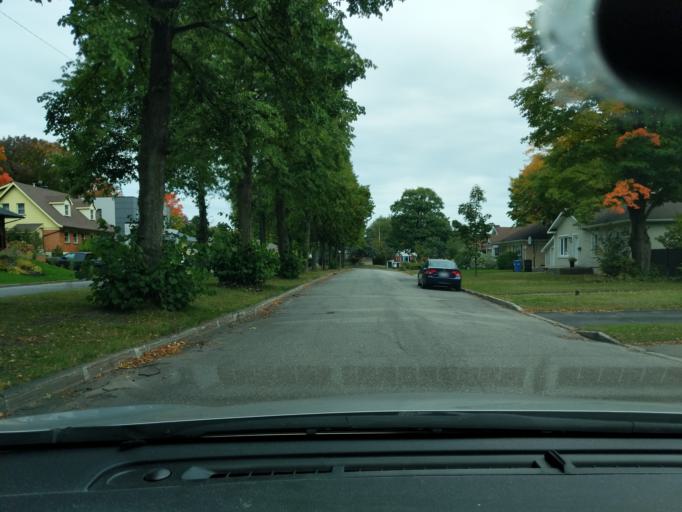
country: CA
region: Quebec
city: L'Ancienne-Lorette
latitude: 46.7711
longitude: -71.2921
